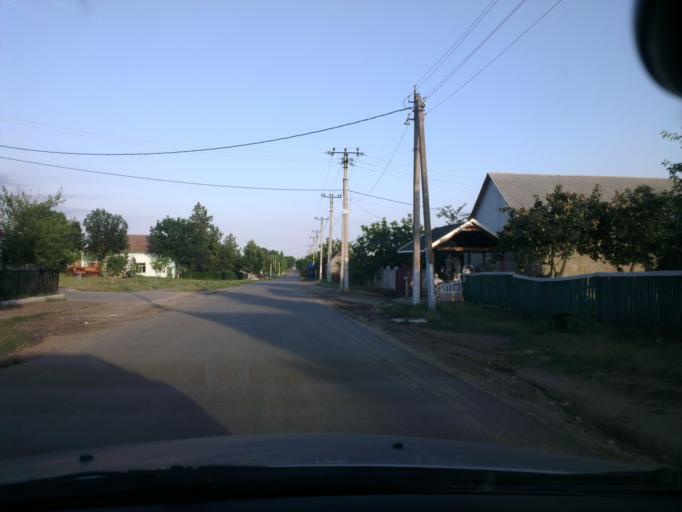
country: MD
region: Cantemir
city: Visniovca
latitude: 46.3560
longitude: 28.4056
